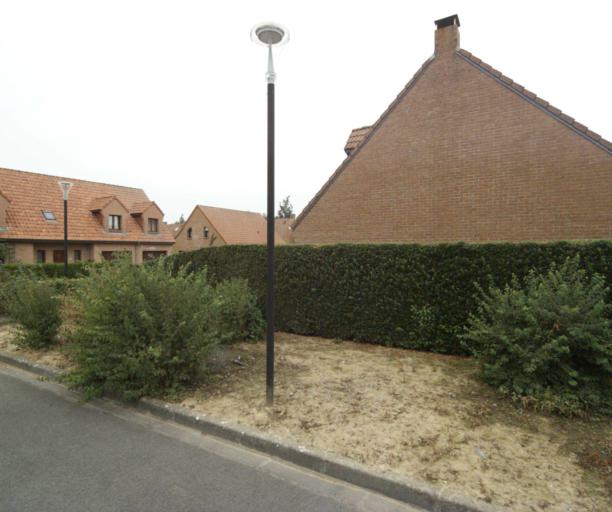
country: FR
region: Nord-Pas-de-Calais
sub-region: Departement du Nord
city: Baisieux
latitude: 50.6144
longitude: 3.2374
